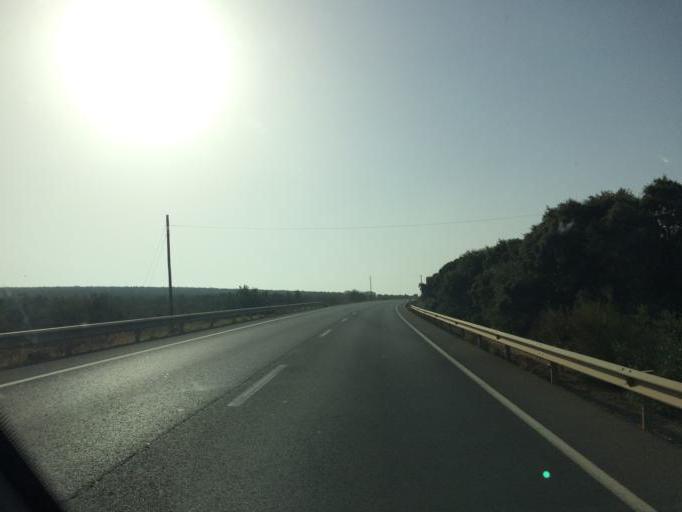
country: ES
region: Andalusia
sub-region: Provincia de Malaga
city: Humilladero
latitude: 37.0584
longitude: -4.6825
